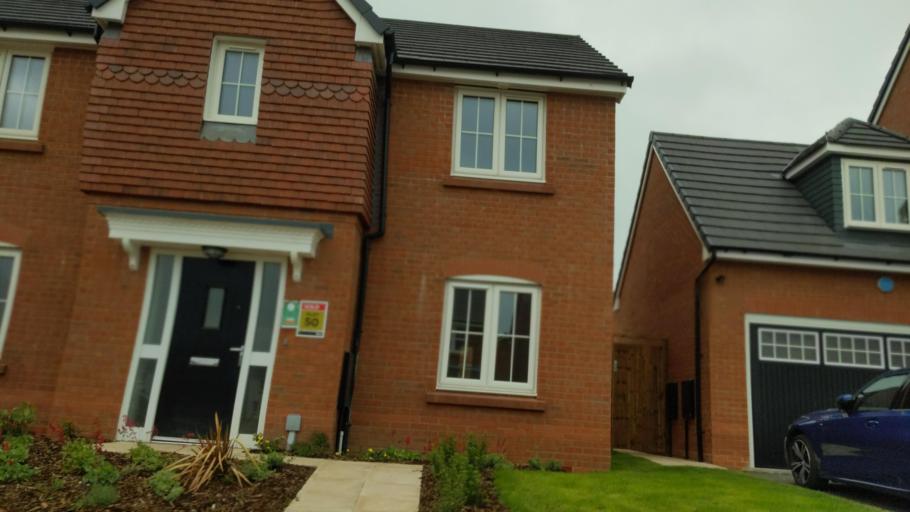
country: GB
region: England
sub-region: Worcestershire
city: Worcester
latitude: 52.1956
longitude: -2.1854
